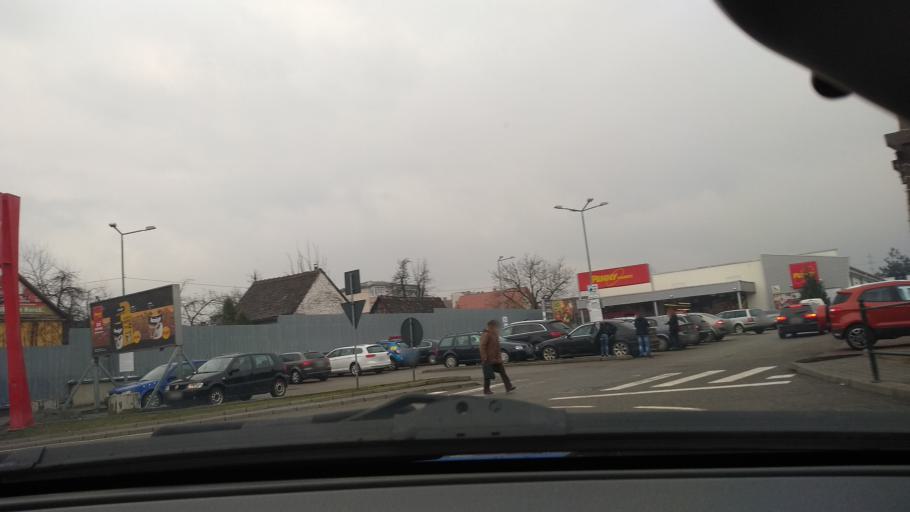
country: RO
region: Mures
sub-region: Oras Sovata
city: Sovata
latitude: 46.5975
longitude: 25.0706
